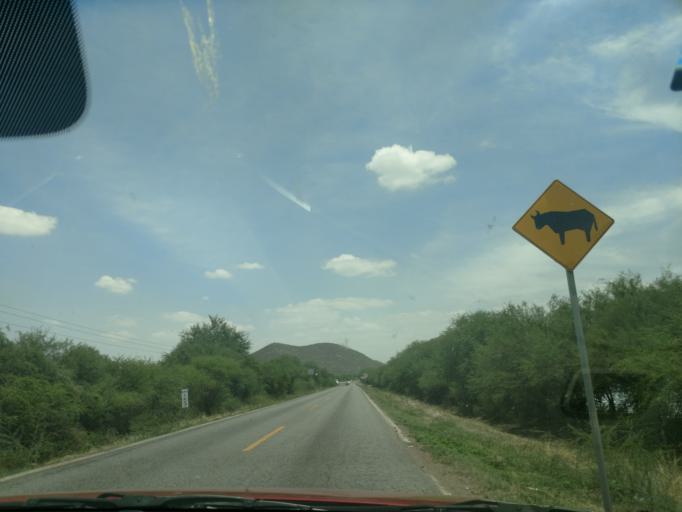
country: MX
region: San Luis Potosi
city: Ciudad Fernandez
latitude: 22.0076
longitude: -100.1514
